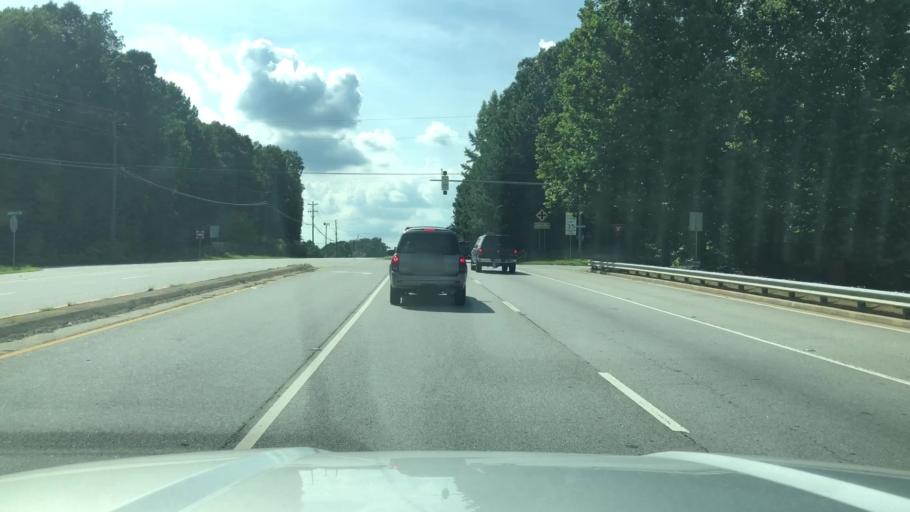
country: US
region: Georgia
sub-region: Douglas County
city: Lithia Springs
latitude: 33.7409
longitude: -84.6798
